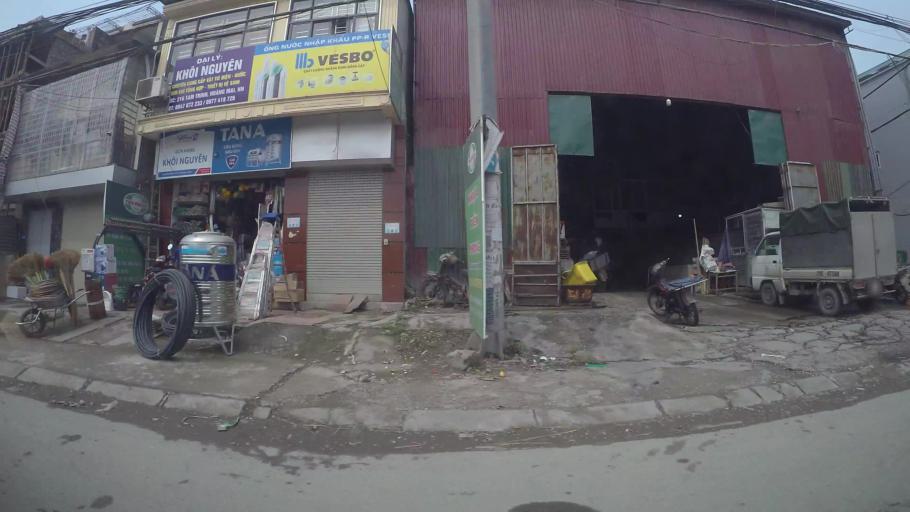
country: VN
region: Ha Noi
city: Van Dien
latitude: 20.9662
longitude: 105.8681
